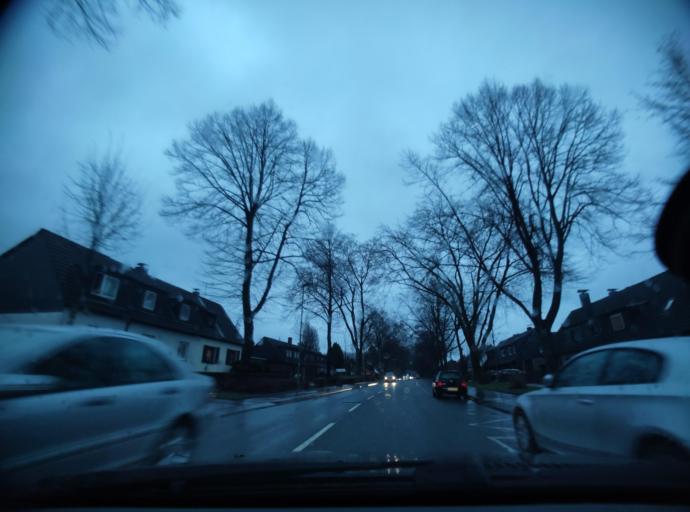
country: DE
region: North Rhine-Westphalia
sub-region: Regierungsbezirk Dusseldorf
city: Essen
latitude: 51.4853
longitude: 7.0246
